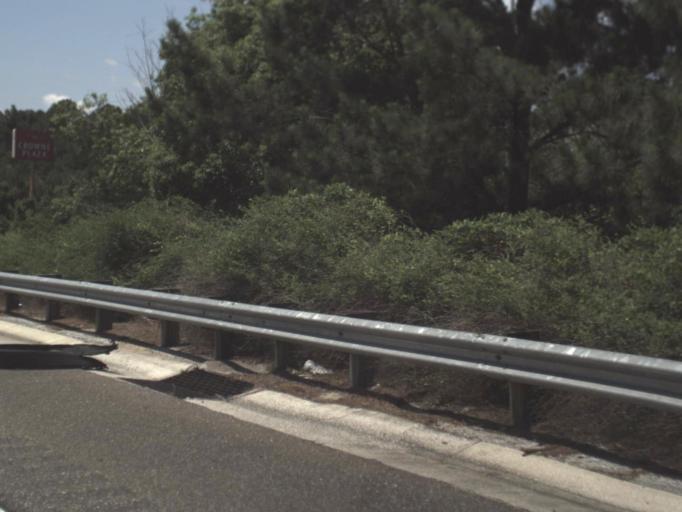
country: US
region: Florida
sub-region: Duval County
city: Jacksonville
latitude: 30.4803
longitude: -81.6441
